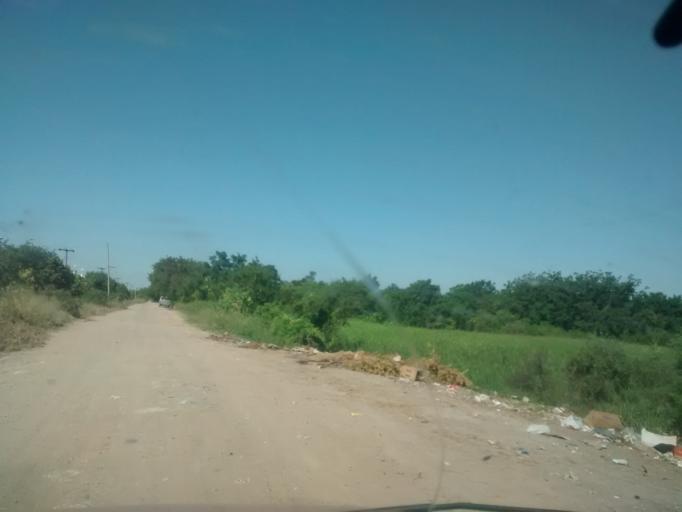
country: AR
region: Chaco
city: Resistencia
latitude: -27.4433
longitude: -58.9635
